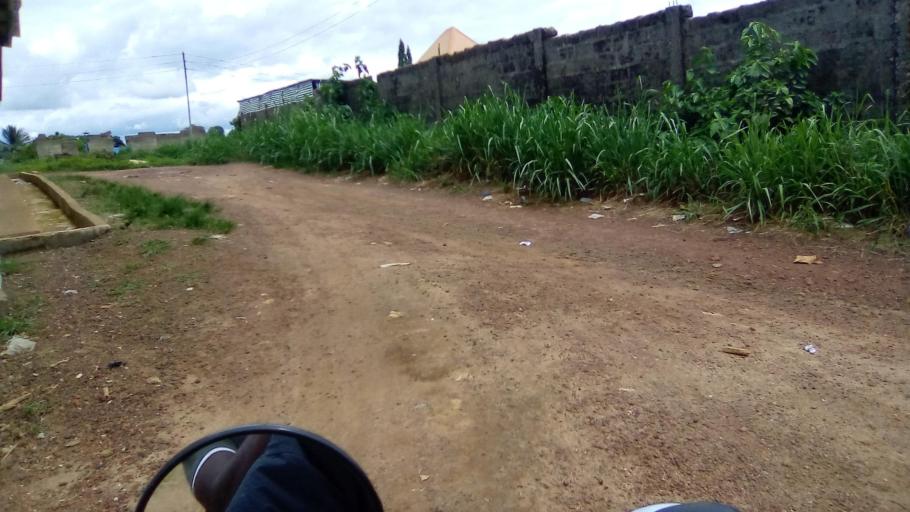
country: SL
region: Southern Province
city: Bo
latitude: 7.9346
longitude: -11.7222
